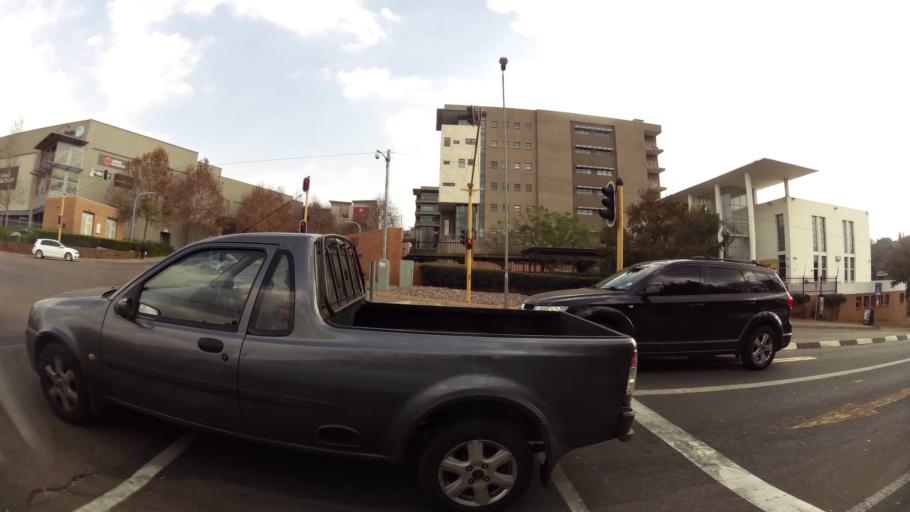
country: ZA
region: Gauteng
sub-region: City of Tshwane Metropolitan Municipality
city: Pretoria
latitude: -25.7651
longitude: 28.2796
